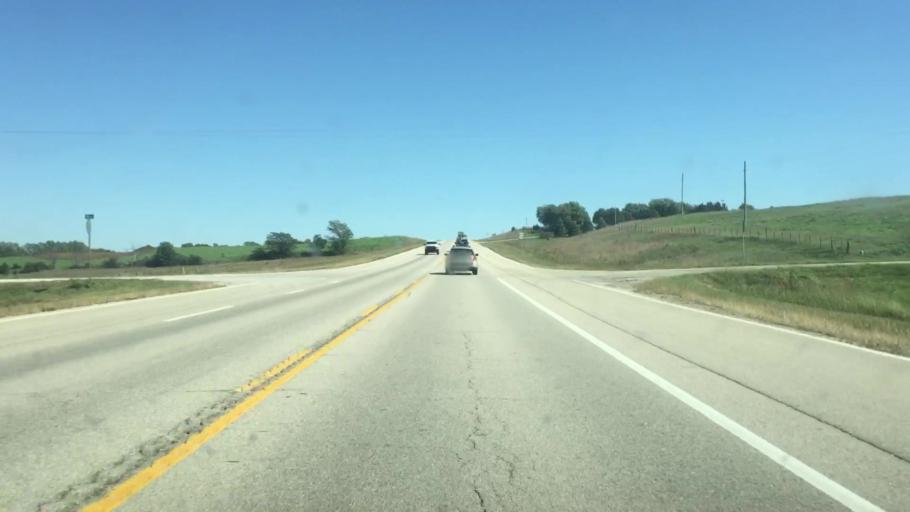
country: US
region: Kansas
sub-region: Nemaha County
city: Seneca
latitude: 39.8411
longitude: -95.9962
